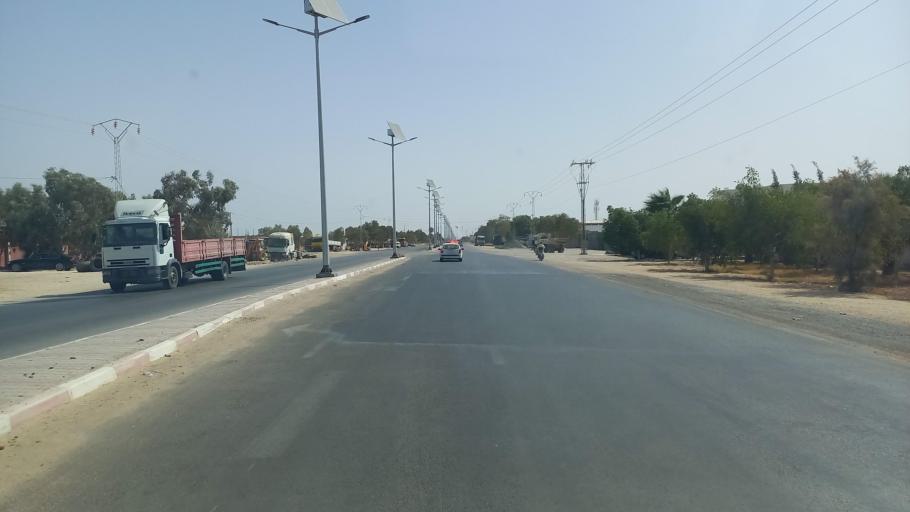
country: TN
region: Madanin
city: Medenine
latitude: 33.3500
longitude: 10.5280
